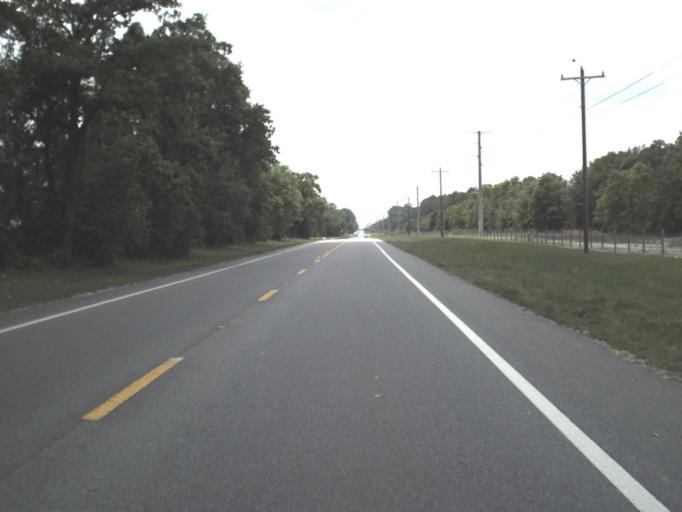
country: US
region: Florida
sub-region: Clay County
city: Keystone Heights
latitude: 29.8821
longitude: -81.9207
